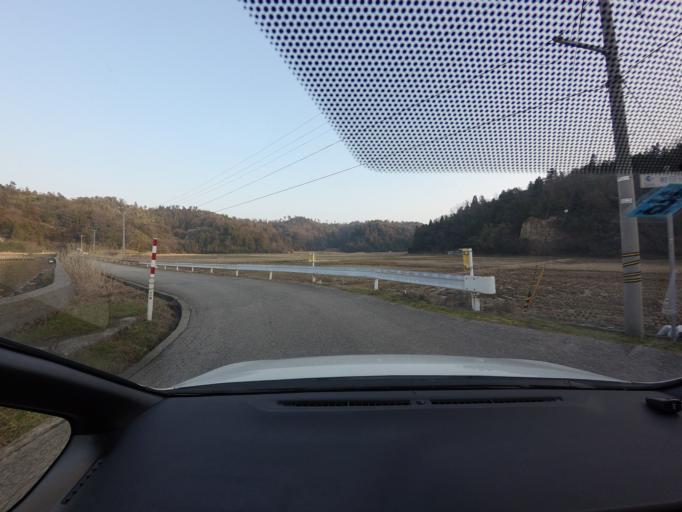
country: JP
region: Ishikawa
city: Nanao
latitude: 37.1425
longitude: 137.0202
